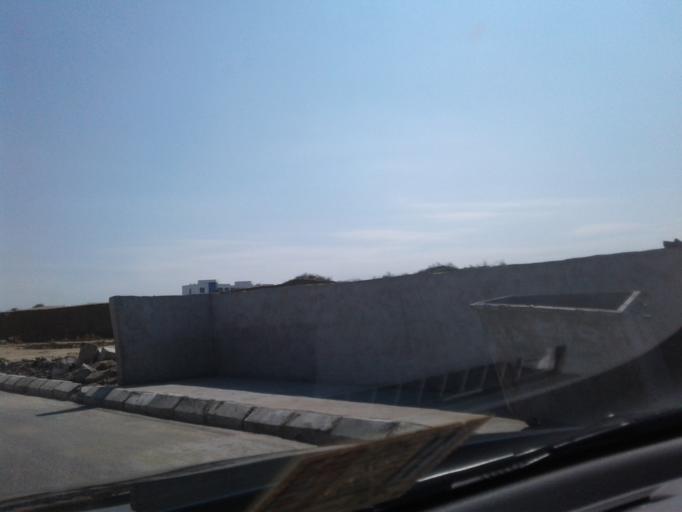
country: TM
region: Ahal
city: Ashgabat
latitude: 38.0103
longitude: 58.3940
